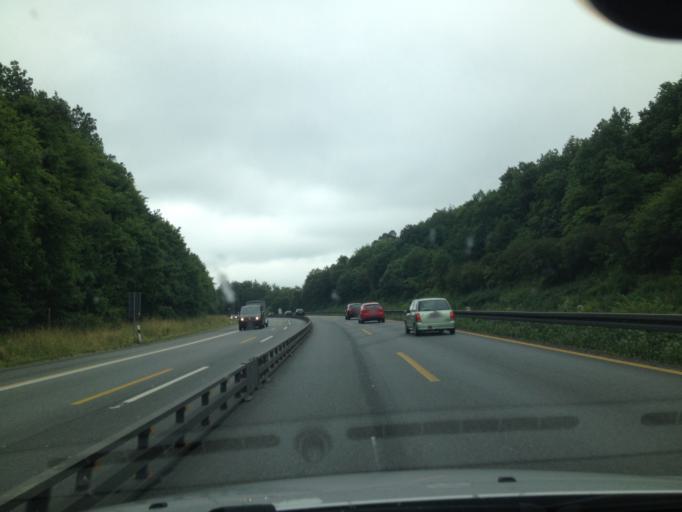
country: DE
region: Hesse
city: Allendorf an der Lahn
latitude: 50.5574
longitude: 8.5636
